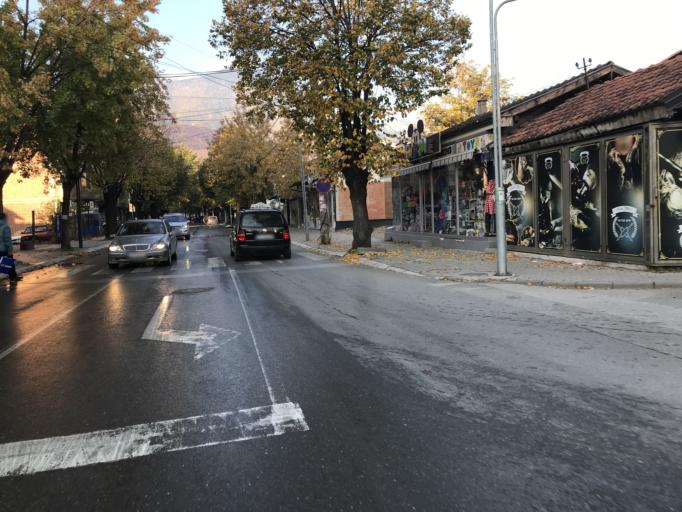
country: XK
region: Pec
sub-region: Komuna e Pejes
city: Peje
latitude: 42.6615
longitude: 20.2939
